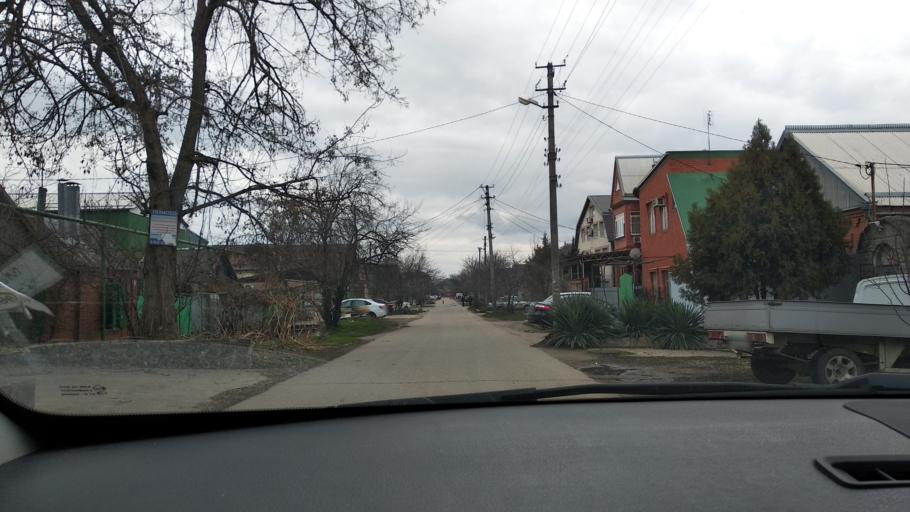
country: RU
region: Krasnodarskiy
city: Krasnodar
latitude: 45.0186
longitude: 39.0069
